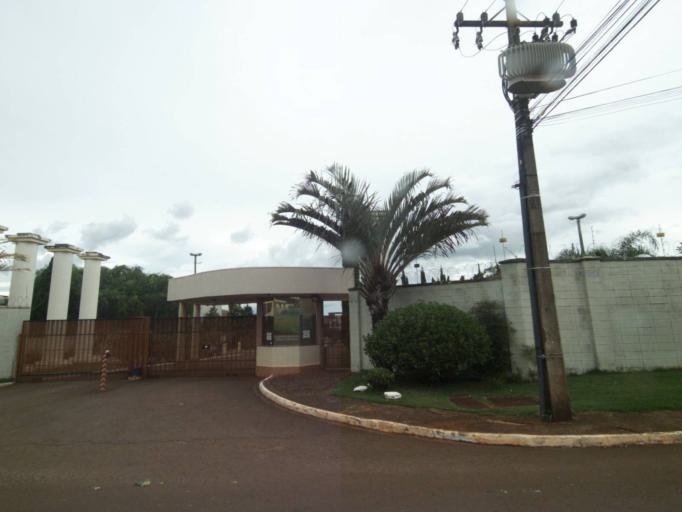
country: BR
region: Parana
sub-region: Campo Mourao
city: Campo Mourao
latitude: -24.0340
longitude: -52.3611
